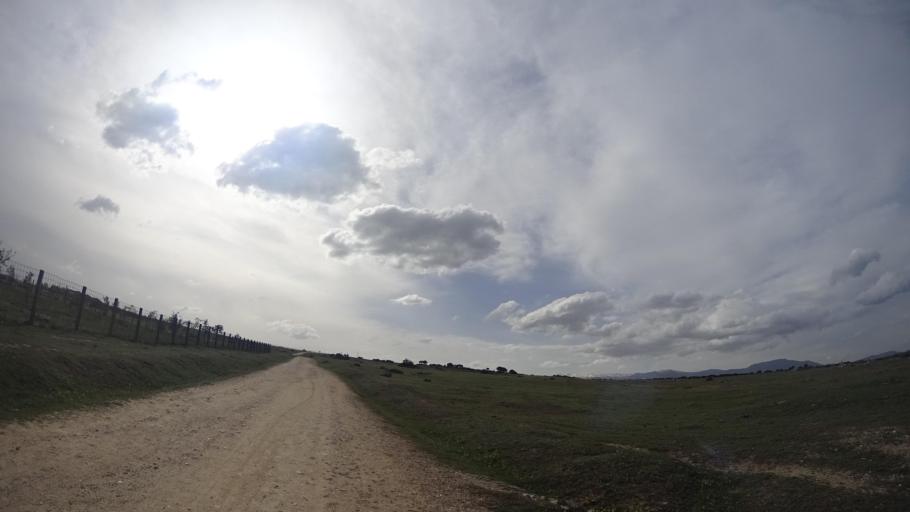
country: ES
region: Madrid
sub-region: Provincia de Madrid
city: Colmenar Viejo
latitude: 40.6992
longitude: -3.7552
